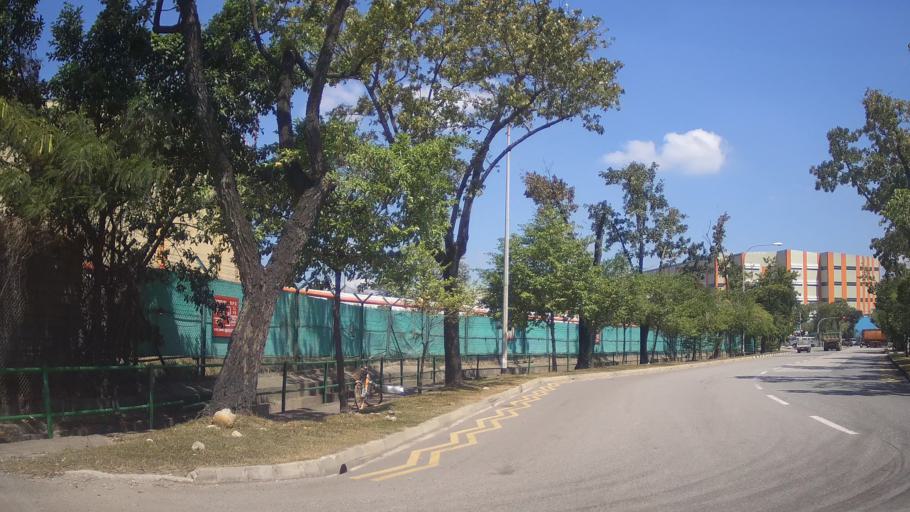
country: SG
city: Singapore
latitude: 1.3137
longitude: 103.6912
